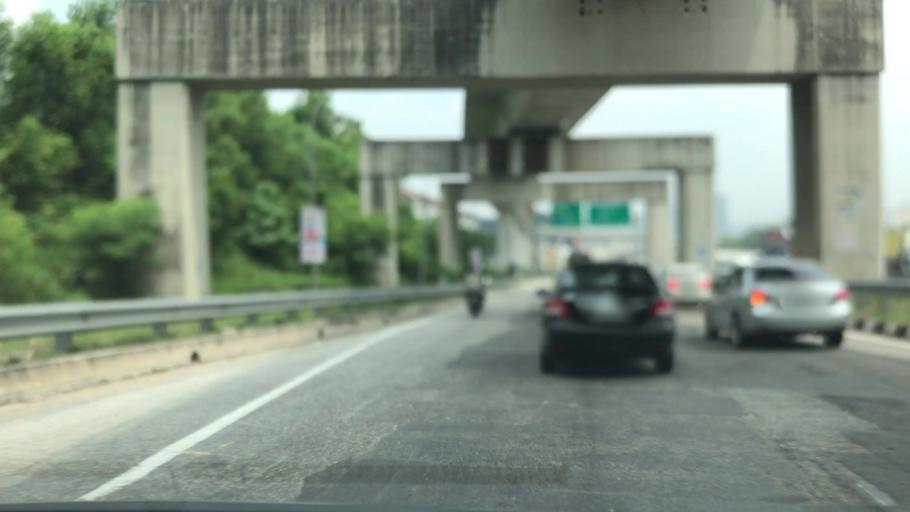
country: MY
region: Selangor
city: Subang Jaya
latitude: 3.0497
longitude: 101.6291
